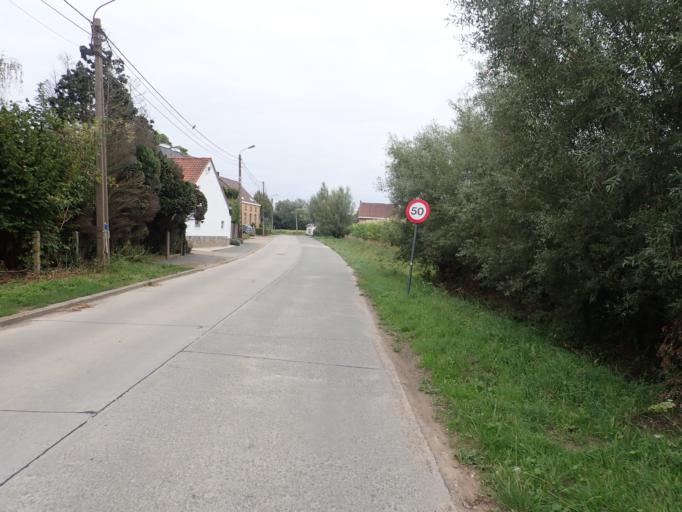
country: BE
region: Flanders
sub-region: Provincie Oost-Vlaanderen
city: Denderleeuw
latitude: 50.9234
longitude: 4.1207
